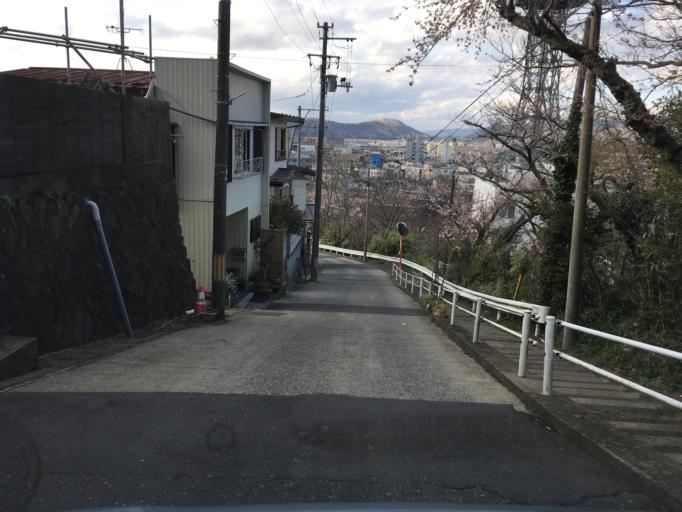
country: JP
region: Miyagi
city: Ishinomaki
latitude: 38.4268
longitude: 141.3070
